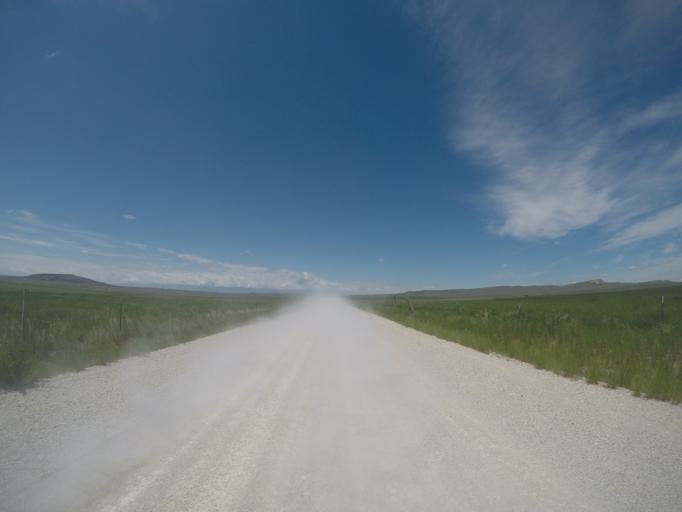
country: US
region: Montana
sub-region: Yellowstone County
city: Laurel
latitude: 45.2196
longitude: -108.7057
